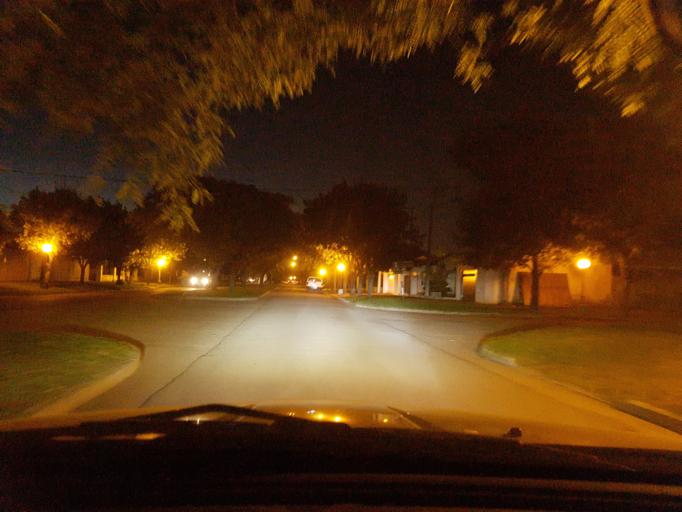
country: AR
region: Cordoba
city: Las Perdices
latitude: -32.7593
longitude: -63.7759
